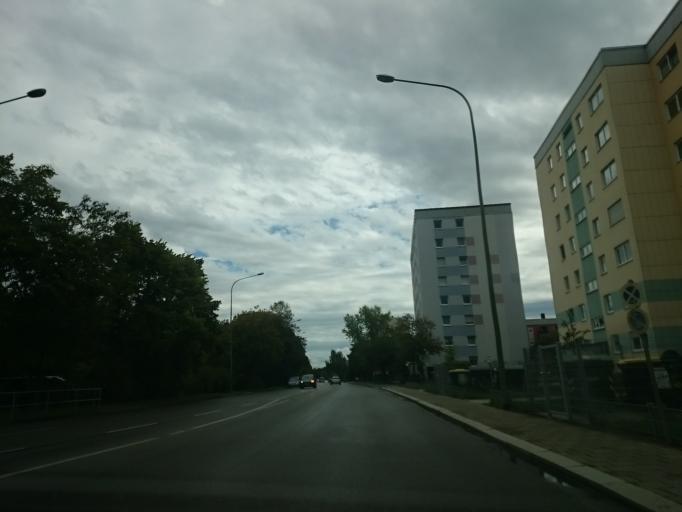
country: DE
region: Bavaria
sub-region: Swabia
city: Konigsbrunn
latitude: 48.2814
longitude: 10.8882
